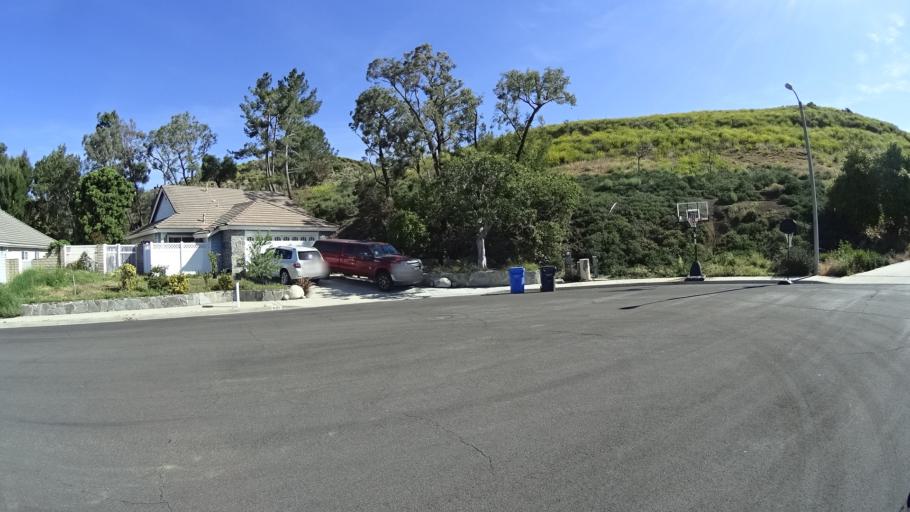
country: US
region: California
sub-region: Ventura County
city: Moorpark
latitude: 34.2291
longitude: -118.8630
